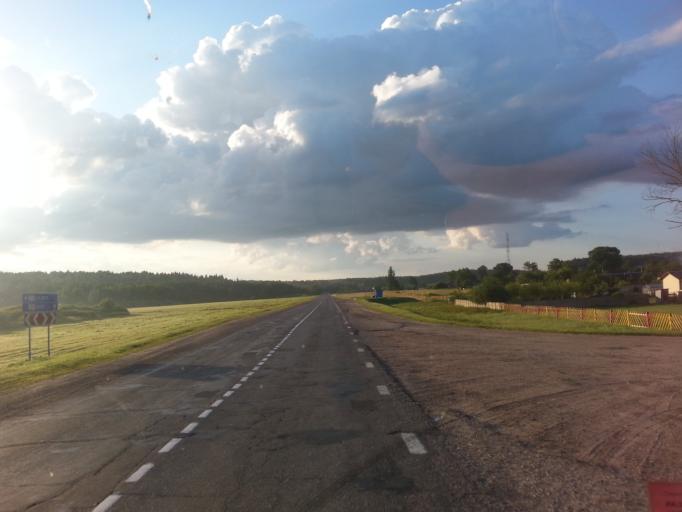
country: BY
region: Minsk
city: Il'ya
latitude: 54.4775
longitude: 27.2567
